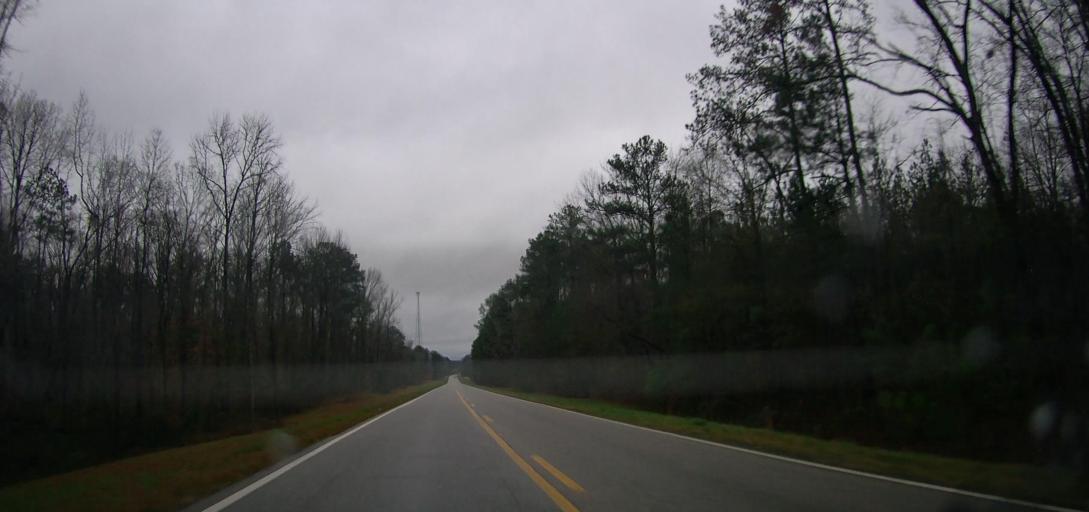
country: US
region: Alabama
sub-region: Bibb County
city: Centreville
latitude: 32.8950
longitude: -86.9896
